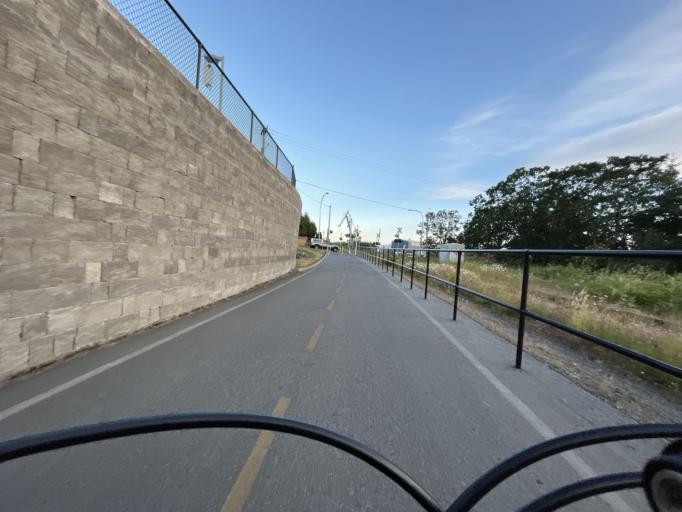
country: CA
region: British Columbia
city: Colwood
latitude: 48.4409
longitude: -123.4295
